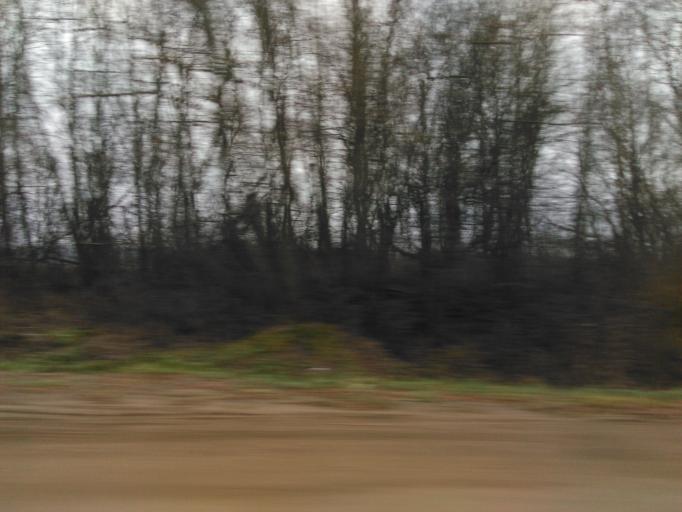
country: RU
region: Moskovskaya
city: Ashukino
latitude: 56.1373
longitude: 37.9853
